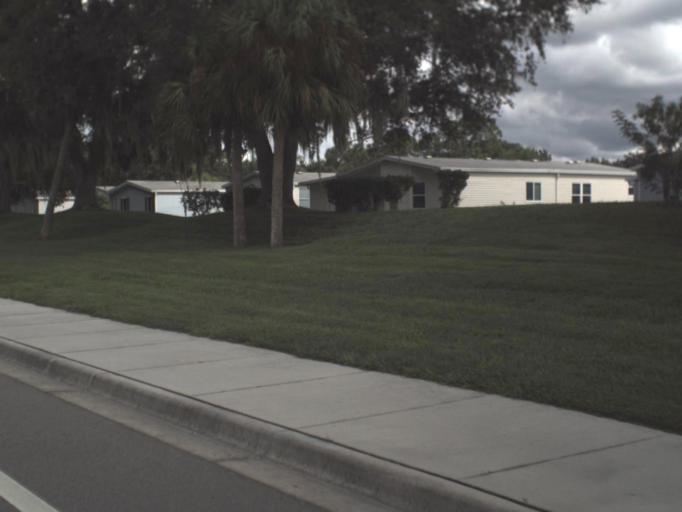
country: US
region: Florida
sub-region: Manatee County
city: Ellenton
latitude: 27.5494
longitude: -82.4640
